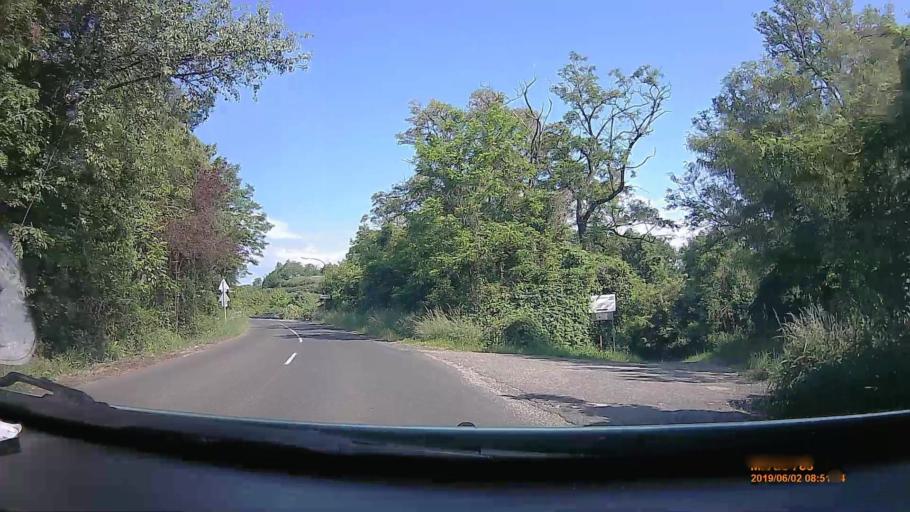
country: HU
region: Borsod-Abauj-Zemplen
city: Sajobabony
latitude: 48.1468
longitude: 20.6874
